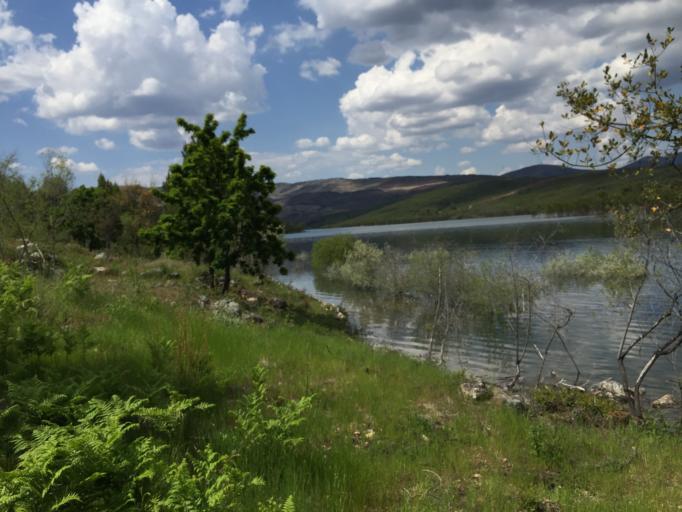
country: PT
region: Coimbra
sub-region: Pampilhosa da Serra
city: Pampilhosa da Serra
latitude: 40.0934
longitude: -7.8585
